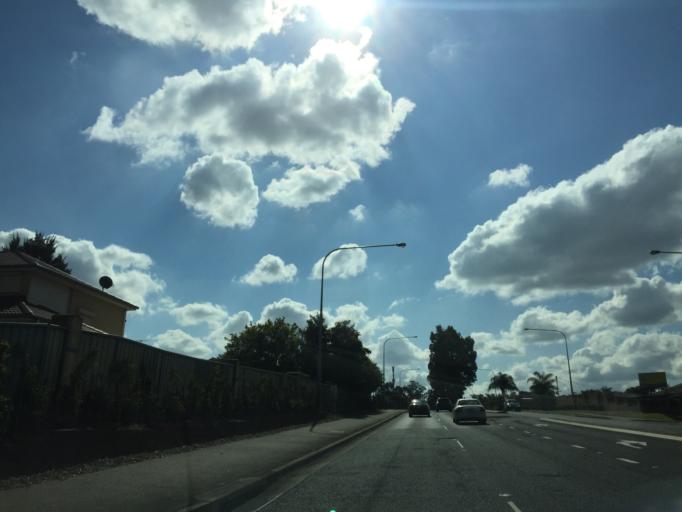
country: AU
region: New South Wales
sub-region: Blacktown
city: Quakers Hill
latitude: -33.7206
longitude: 150.8922
